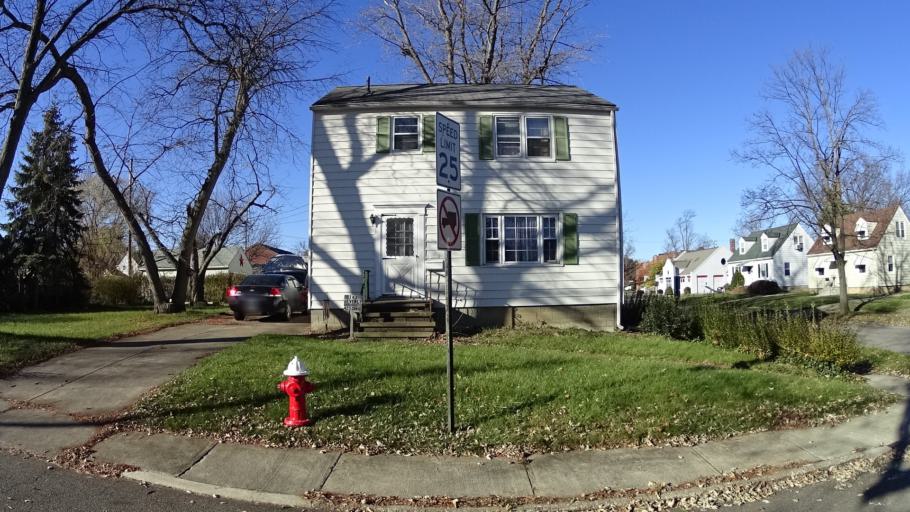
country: US
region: Ohio
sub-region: Lorain County
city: Elyria
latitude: 41.3750
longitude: -82.0930
